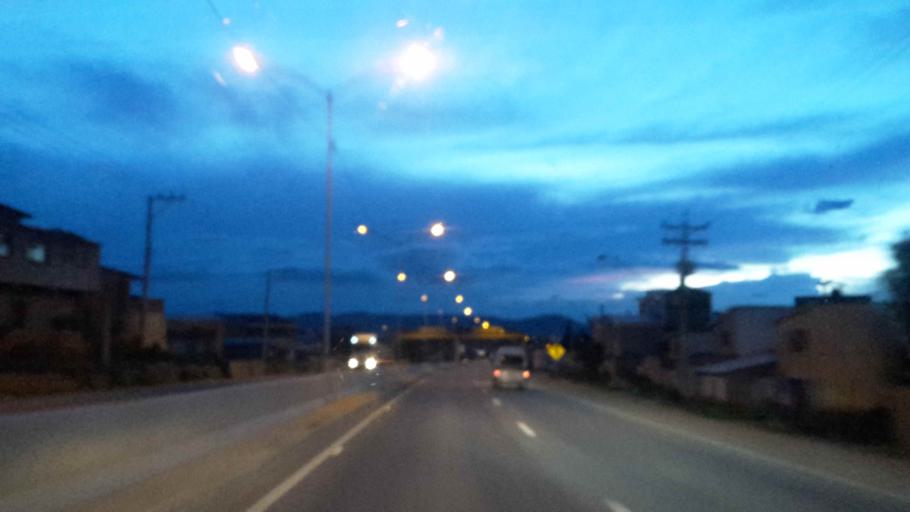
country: BO
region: Cochabamba
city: Colomi
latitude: -17.4068
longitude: -65.9853
